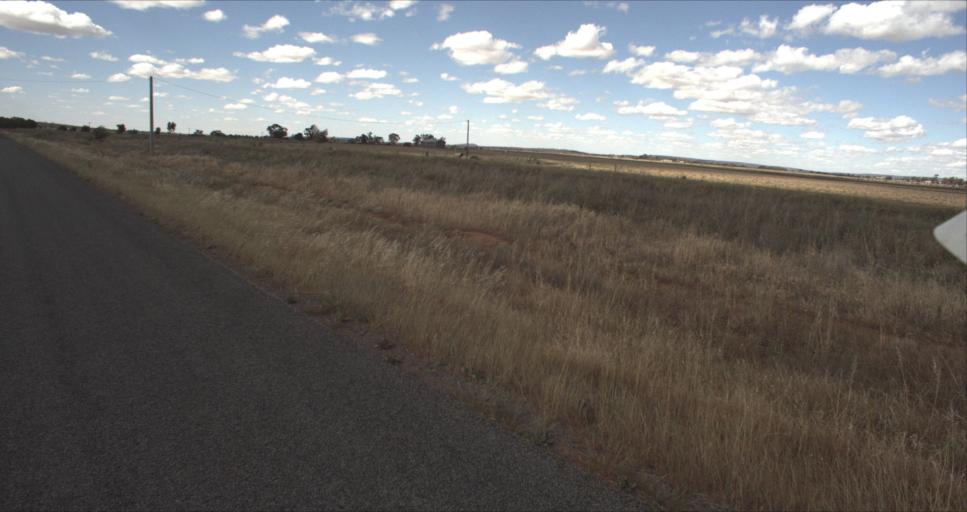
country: AU
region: New South Wales
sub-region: Leeton
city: Leeton
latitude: -34.4505
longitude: 146.2546
